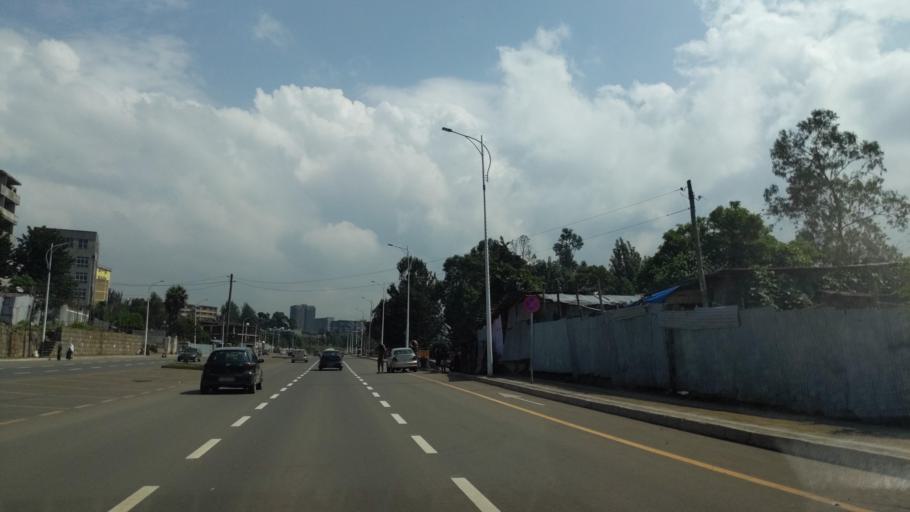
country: ET
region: Adis Abeba
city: Addis Ababa
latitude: 9.0013
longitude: 38.7736
